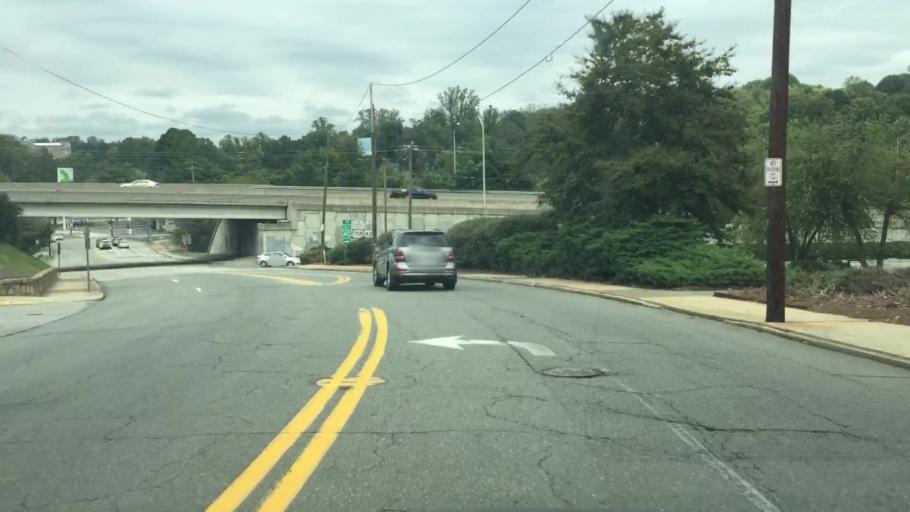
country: US
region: North Carolina
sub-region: Forsyth County
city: Winston-Salem
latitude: 36.0907
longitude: -80.2654
